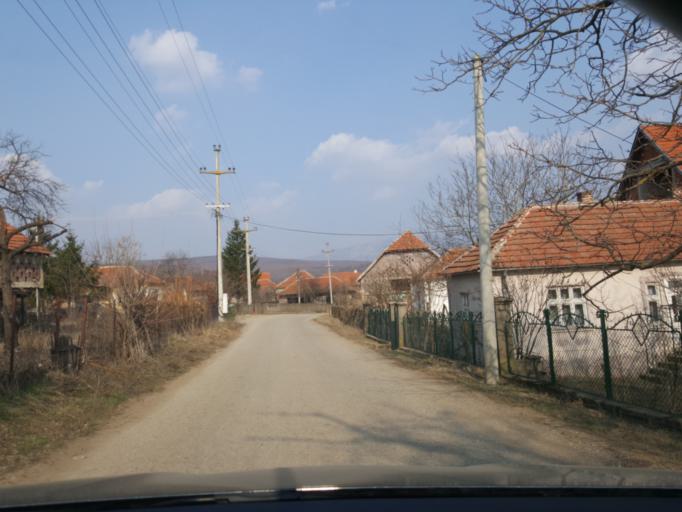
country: RS
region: Central Serbia
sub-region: Nisavski Okrug
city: Aleksinac
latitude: 43.5281
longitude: 21.7362
